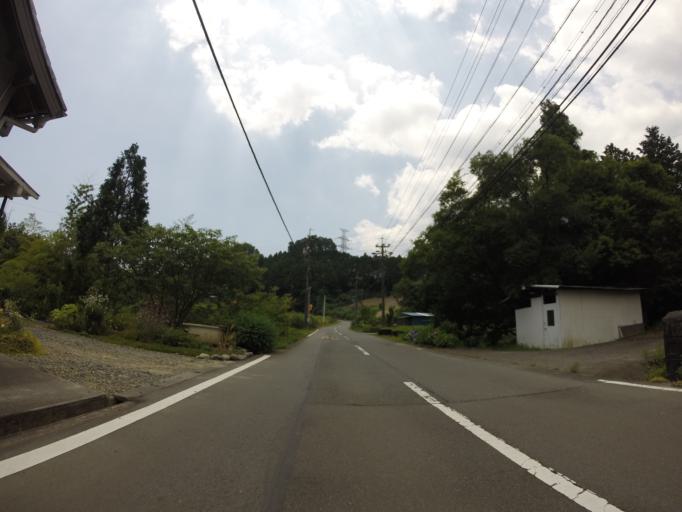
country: JP
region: Shizuoka
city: Kanaya
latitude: 34.8191
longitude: 138.0676
